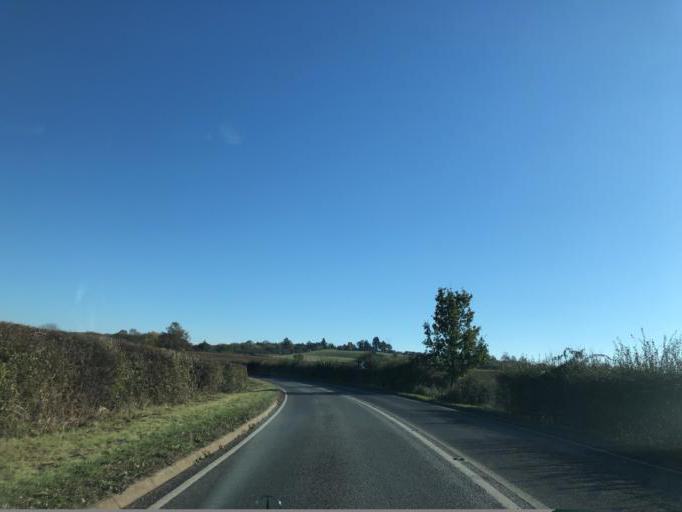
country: GB
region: England
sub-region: Warwickshire
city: Harbury
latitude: 52.2614
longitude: -1.4576
